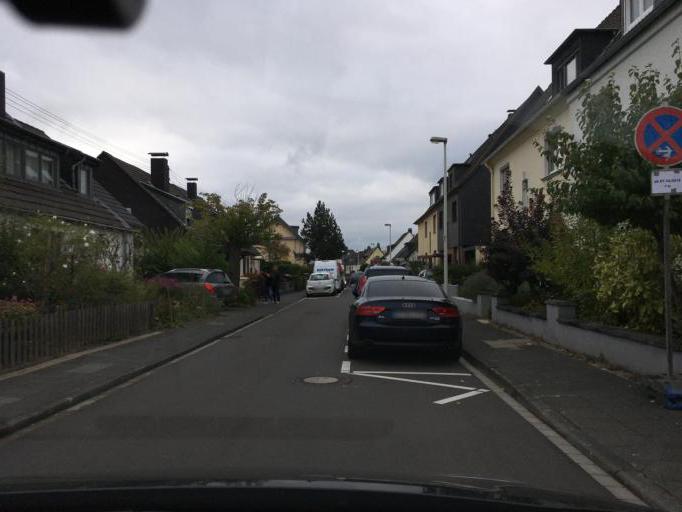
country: DE
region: North Rhine-Westphalia
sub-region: Regierungsbezirk Koln
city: Bonn
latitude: 50.7475
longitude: 7.1344
